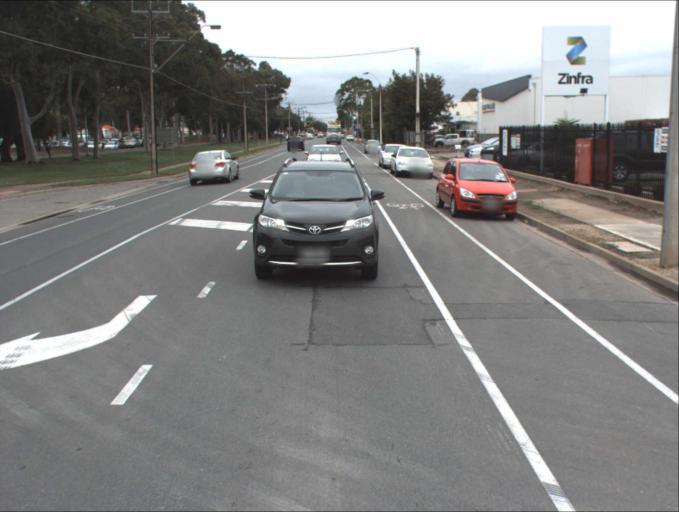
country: AU
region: South Australia
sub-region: Charles Sturt
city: Woodville
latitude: -34.8726
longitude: 138.5661
